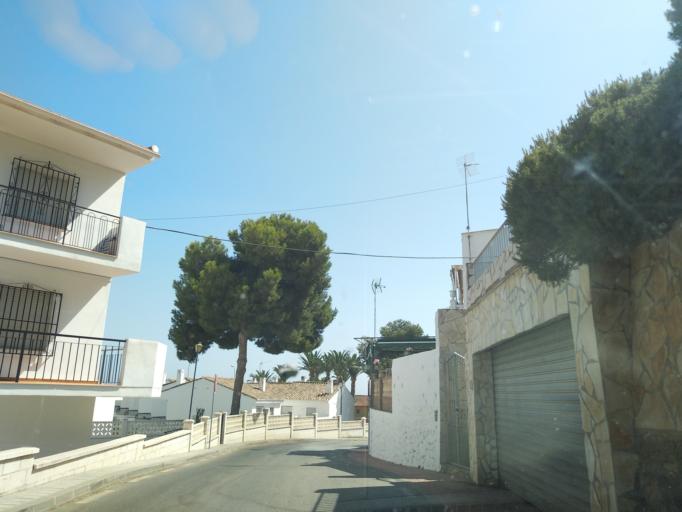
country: ES
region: Andalusia
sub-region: Provincia de Malaga
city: Valdes
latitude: 36.7165
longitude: -4.2002
